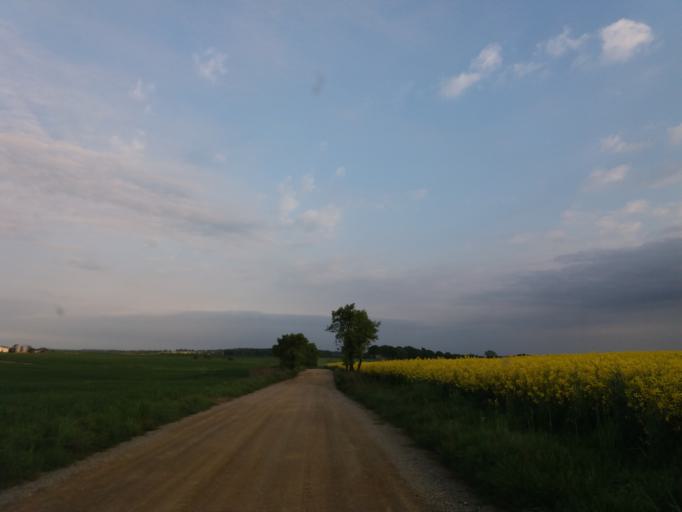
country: PL
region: West Pomeranian Voivodeship
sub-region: Powiat choszczenski
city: Pelczyce
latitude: 53.0350
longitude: 15.2603
